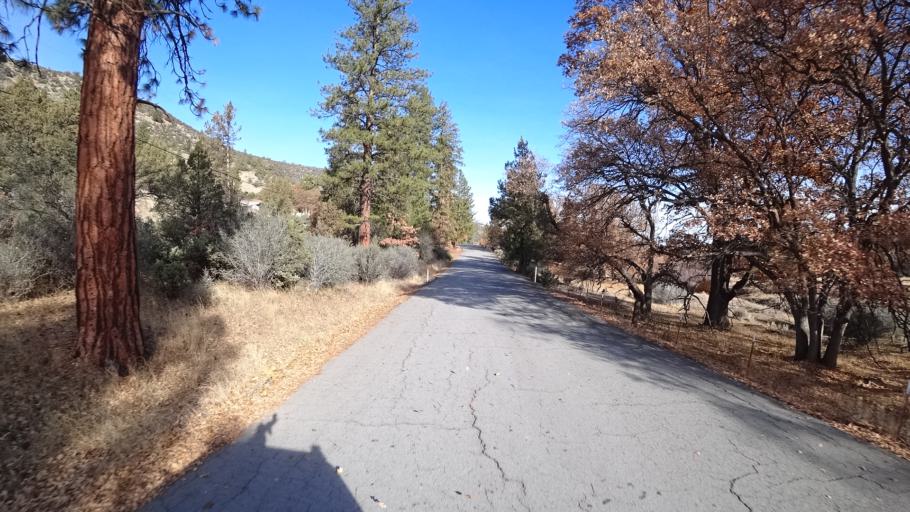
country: US
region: California
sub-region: Siskiyou County
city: Montague
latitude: 41.6156
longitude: -122.5779
